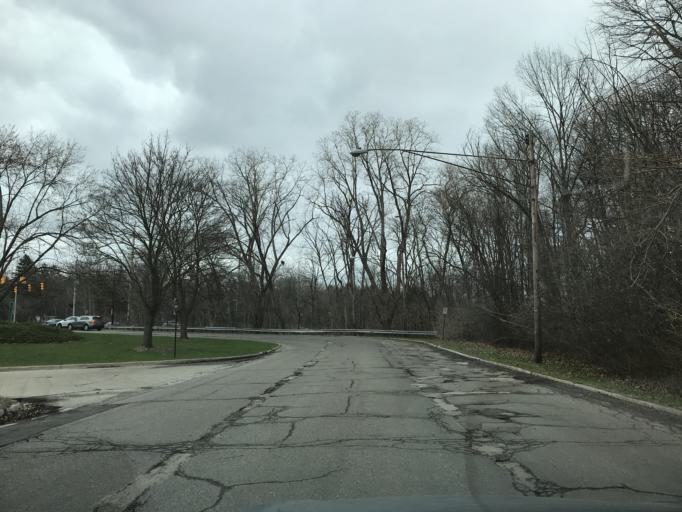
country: US
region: Michigan
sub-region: Washtenaw County
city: Ann Arbor
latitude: 42.2583
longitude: -83.7100
